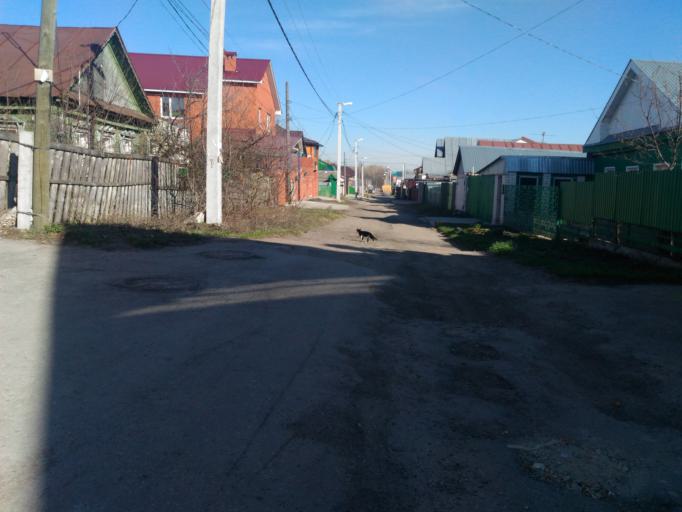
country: RU
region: Ulyanovsk
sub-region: Ulyanovskiy Rayon
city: Ulyanovsk
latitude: 54.3528
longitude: 48.3767
